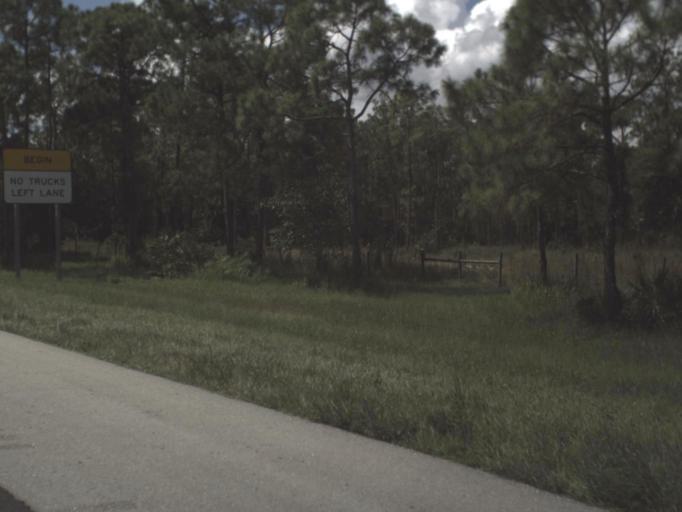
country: US
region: Florida
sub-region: Lee County
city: Gateway
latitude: 26.5832
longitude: -81.7949
